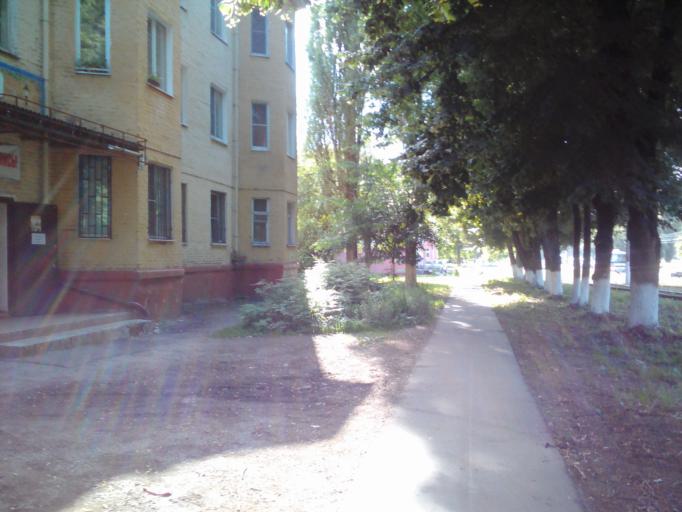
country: RU
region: Kursk
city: Voroshnevo
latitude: 51.6665
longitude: 36.1054
